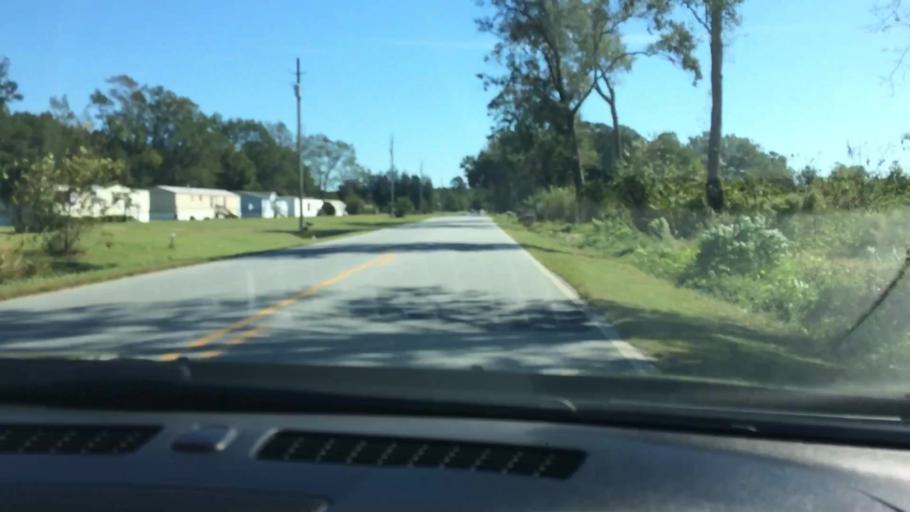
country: US
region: North Carolina
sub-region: Pitt County
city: Grifton
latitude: 35.3767
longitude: -77.3632
